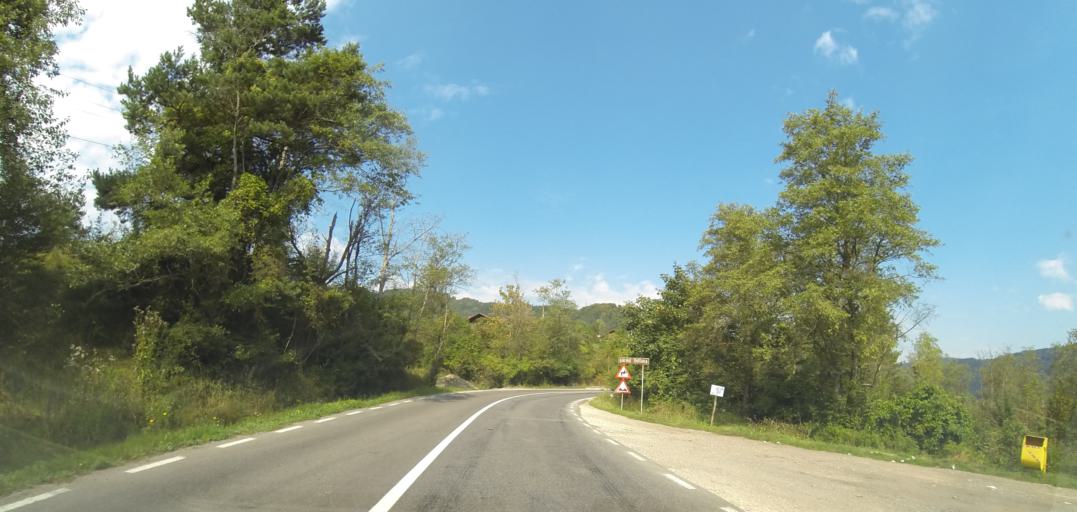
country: RO
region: Brasov
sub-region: Comuna Tarlungeni
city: Tarlungeni
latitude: 45.5597
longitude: 25.7729
